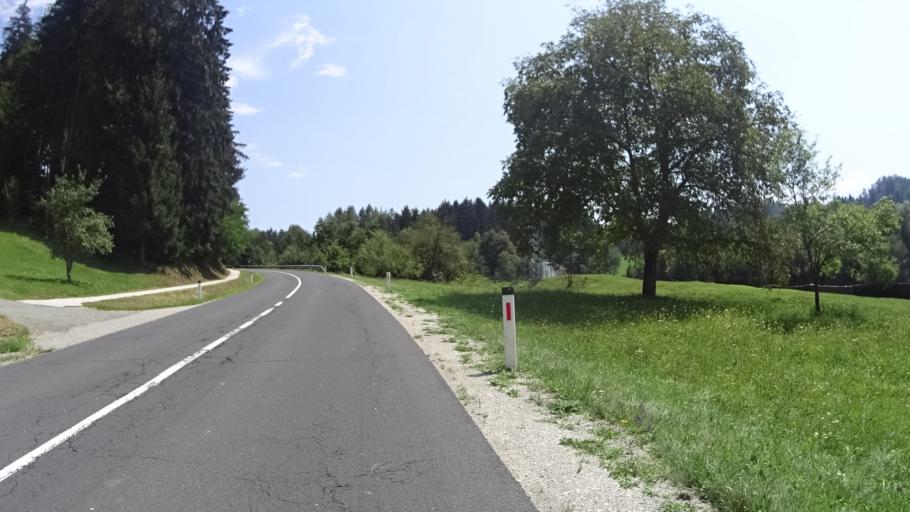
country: SI
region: Mezica
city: Mezica
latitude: 46.5647
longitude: 14.8449
